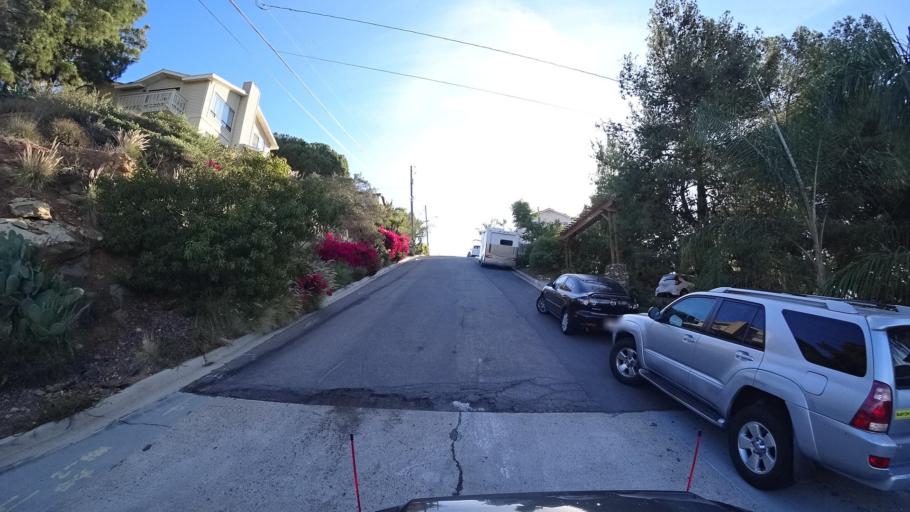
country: US
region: California
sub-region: San Diego County
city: La Presa
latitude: 32.7202
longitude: -116.9882
